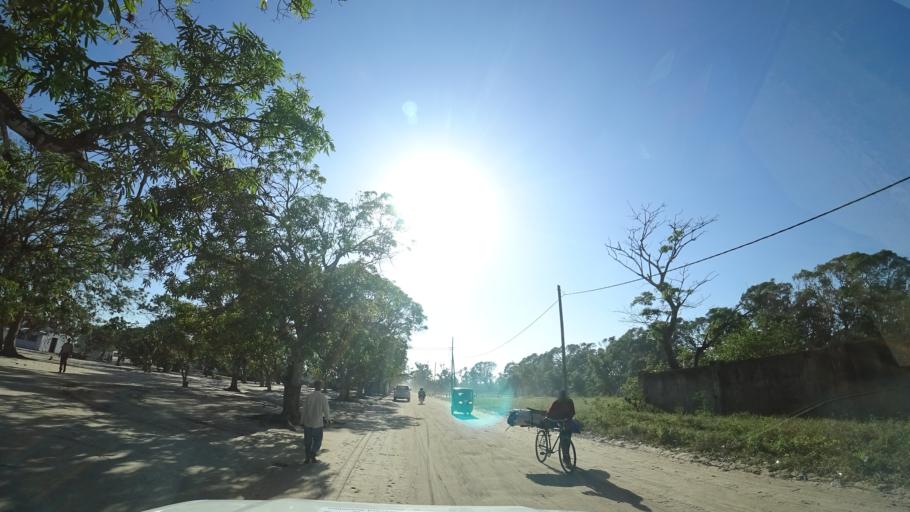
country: MZ
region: Sofala
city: Beira
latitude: -19.7680
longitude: 34.8921
